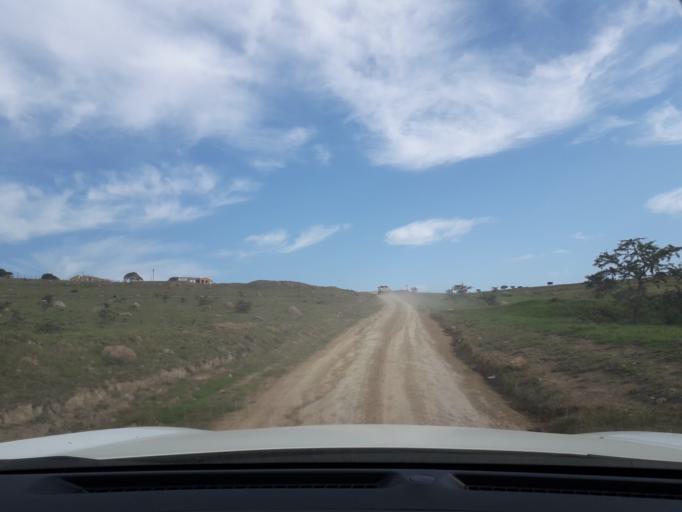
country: ZA
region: Eastern Cape
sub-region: Buffalo City Metropolitan Municipality
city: Bhisho
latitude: -32.9973
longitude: 27.3354
